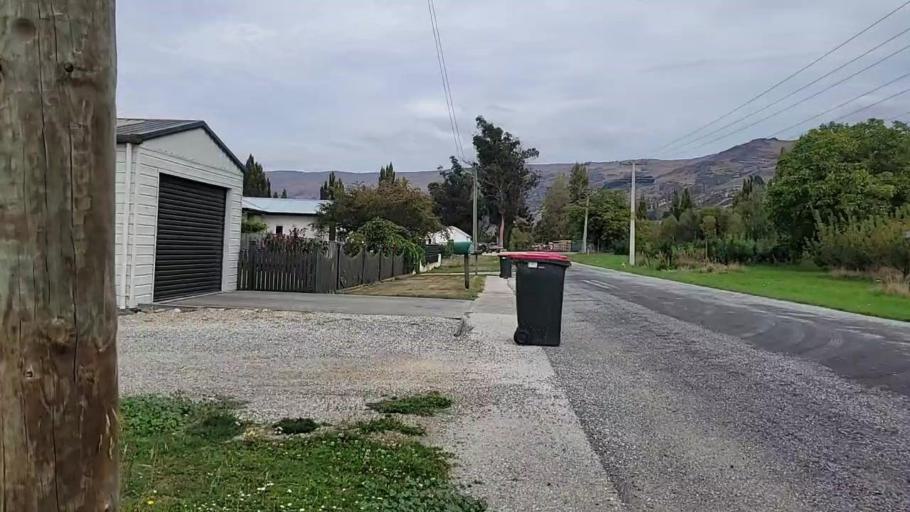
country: NZ
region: Otago
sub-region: Queenstown-Lakes District
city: Kingston
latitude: -45.4815
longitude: 169.3125
